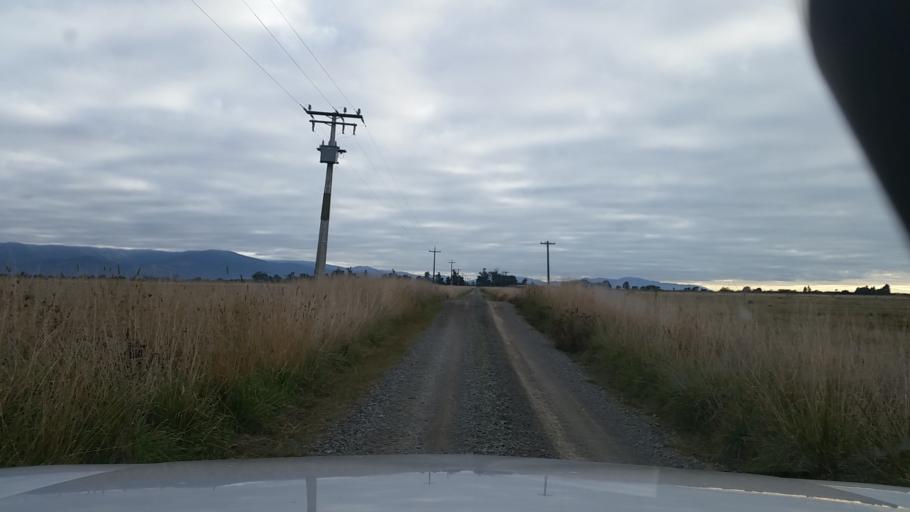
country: NZ
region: Marlborough
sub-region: Marlborough District
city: Blenheim
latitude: -41.5086
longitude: 174.0294
